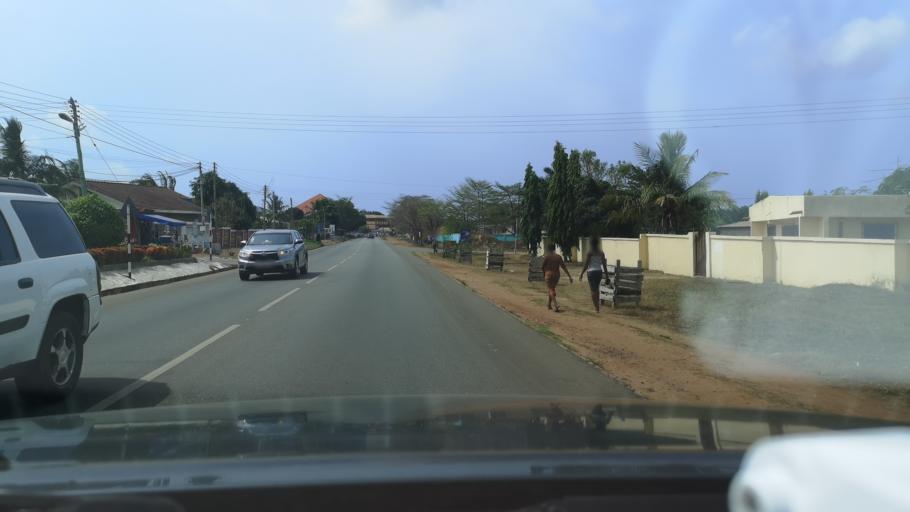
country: GH
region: Greater Accra
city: Tema
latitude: 5.6709
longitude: -0.0282
